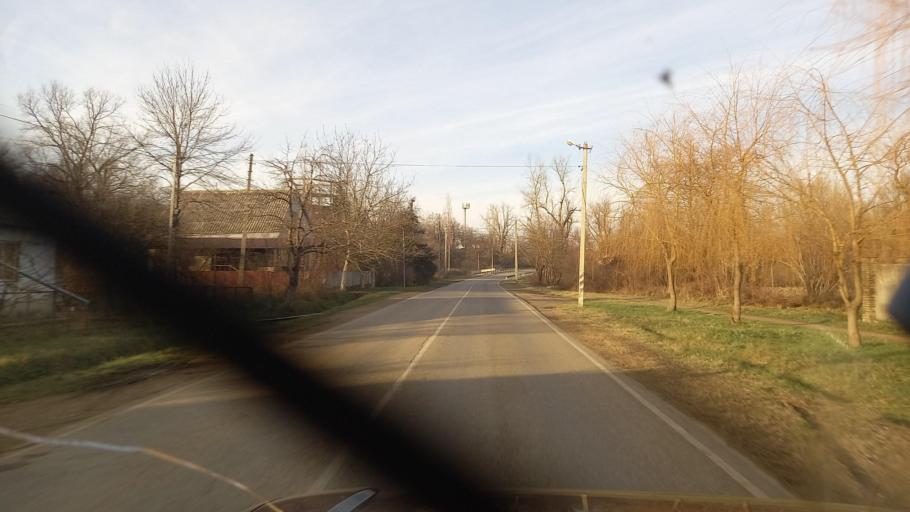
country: RU
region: Krasnodarskiy
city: Khadyzhensk
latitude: 44.4404
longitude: 39.5255
